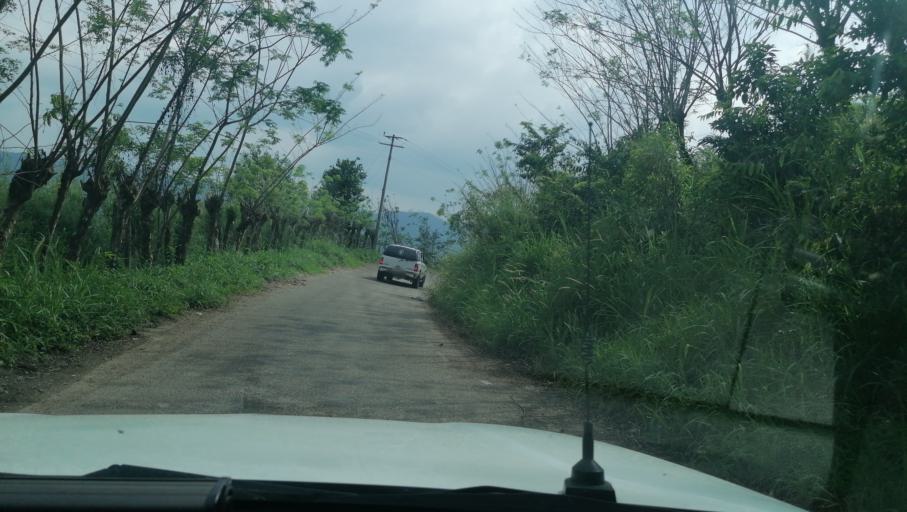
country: MX
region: Chiapas
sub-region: Francisco Leon
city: San Miguel la Sardina
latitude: 17.2340
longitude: -93.3323
